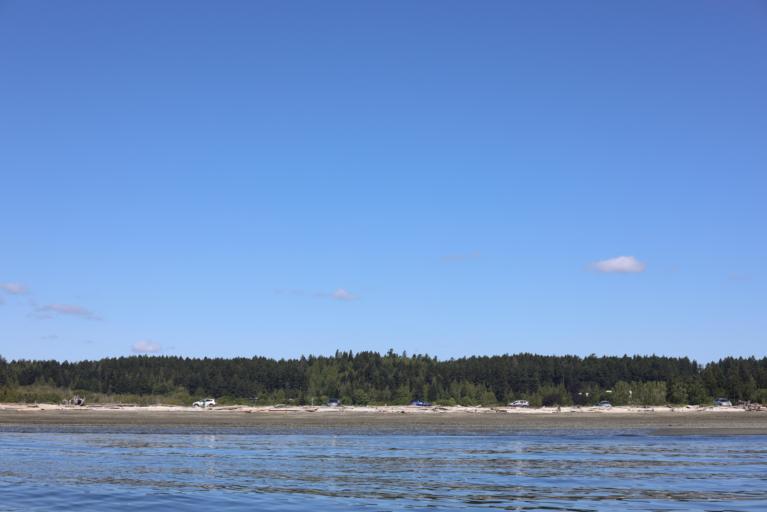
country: CA
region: British Columbia
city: Colwood
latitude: 48.4244
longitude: -123.4614
